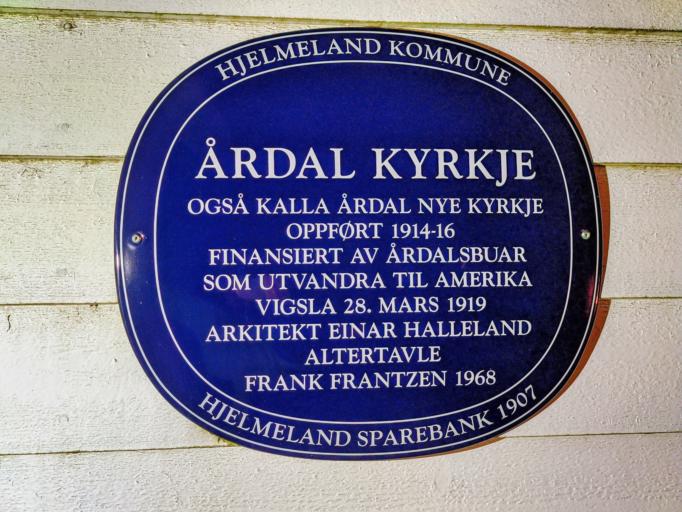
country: NO
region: Rogaland
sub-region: Hjelmeland
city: Hjelmelandsvagen
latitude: 59.1545
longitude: 6.1906
